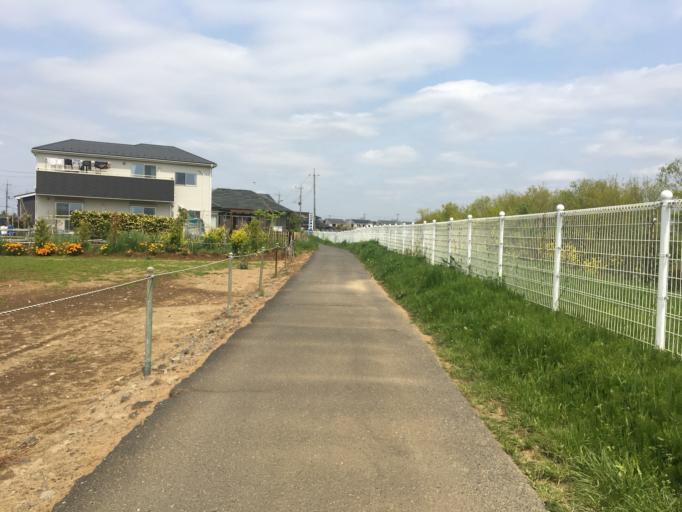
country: JP
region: Saitama
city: Kamifukuoka
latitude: 35.8876
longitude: 139.5487
